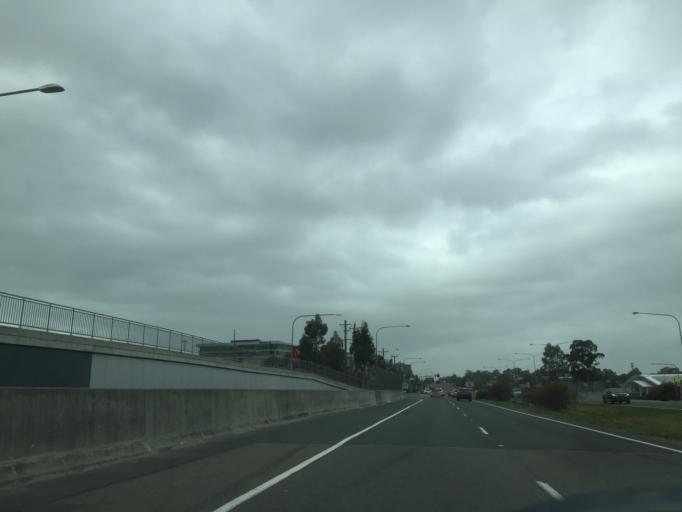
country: AU
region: New South Wales
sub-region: Blacktown
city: Stanhope Gardens
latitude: -33.7307
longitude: 150.9425
